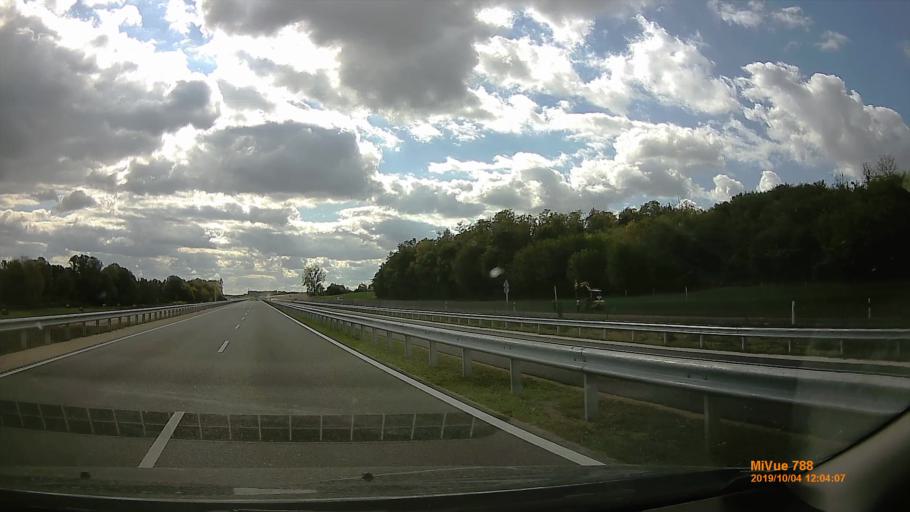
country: HU
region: Somogy
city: Karad
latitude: 46.5787
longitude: 17.8053
